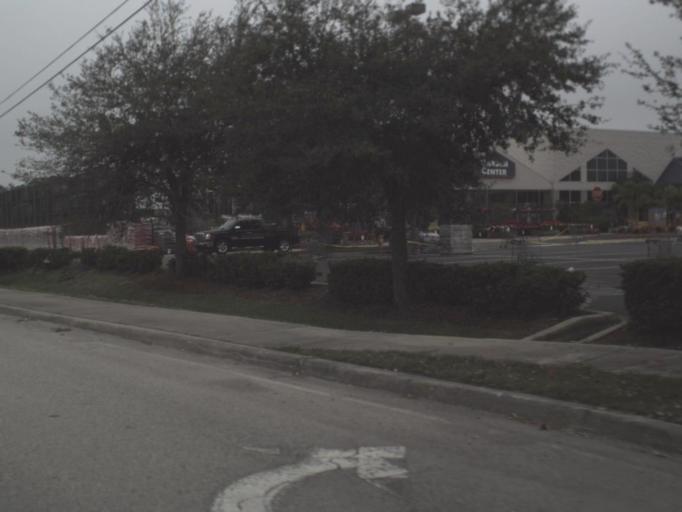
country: US
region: Florida
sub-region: Brevard County
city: June Park
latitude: 28.0773
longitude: -80.6726
